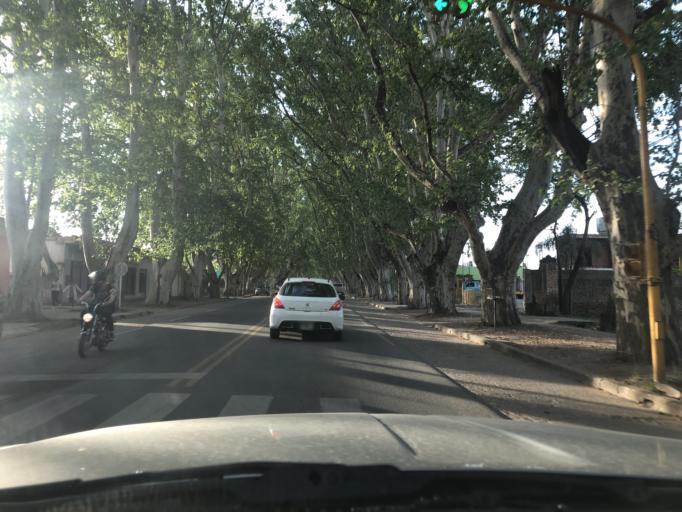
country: AR
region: Cordoba
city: Jesus Maria
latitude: -30.9959
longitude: -64.0914
